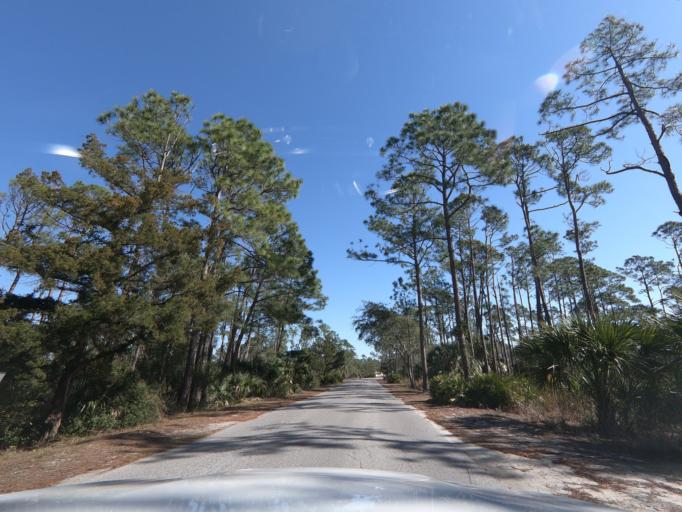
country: US
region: Florida
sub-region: Bay County
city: Lower Grand Lagoon
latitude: 30.1359
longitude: -85.7411
